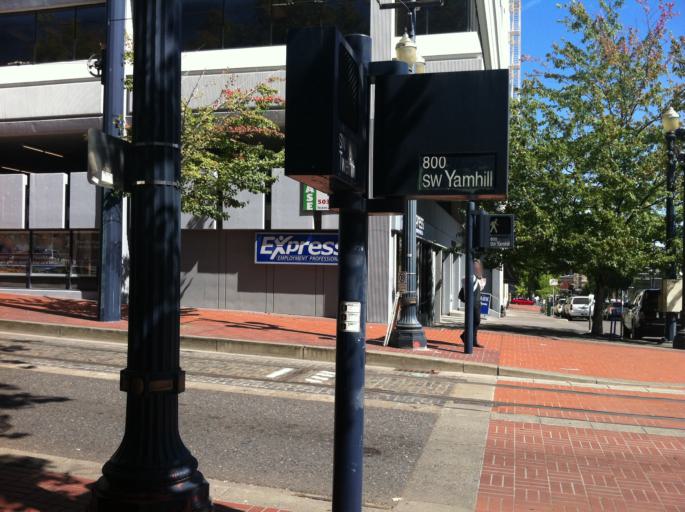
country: US
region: Oregon
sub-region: Multnomah County
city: Portland
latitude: 45.5199
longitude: -122.6847
